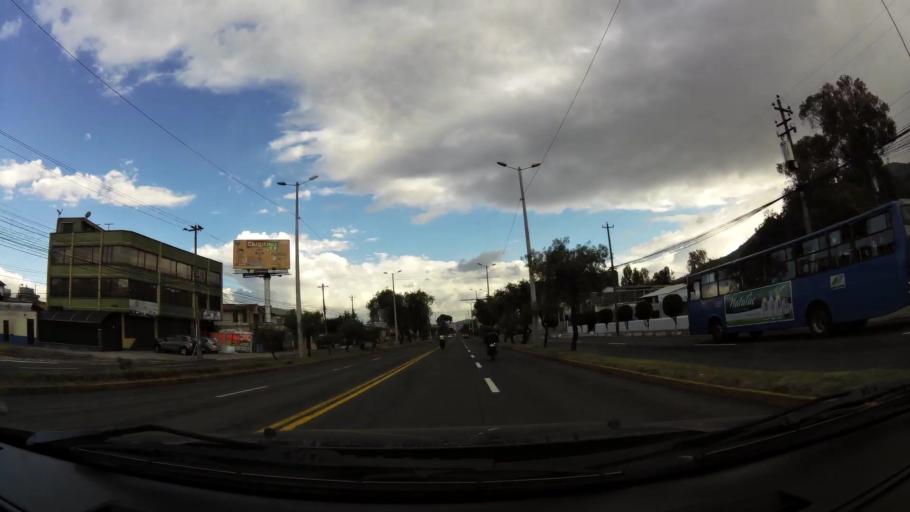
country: EC
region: Pichincha
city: Quito
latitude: -0.1431
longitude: -78.4832
